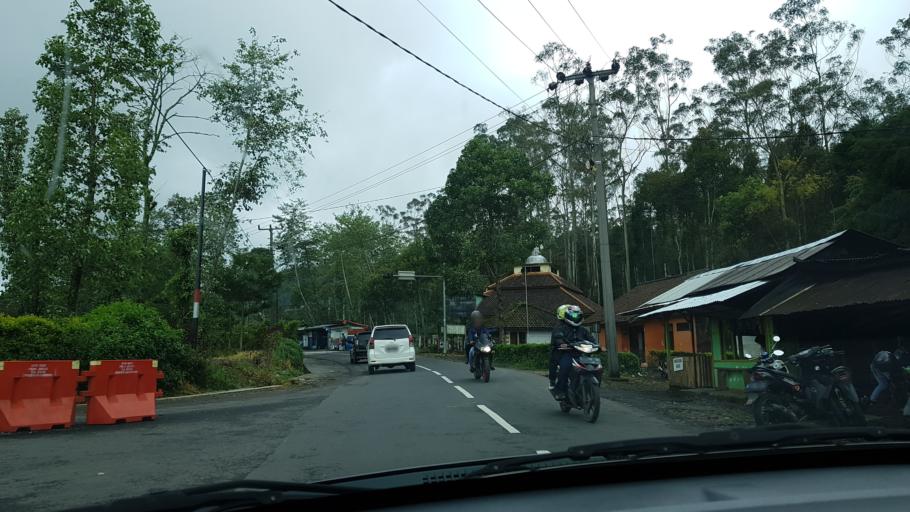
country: ID
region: West Java
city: Banjar
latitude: -7.1540
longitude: 107.3718
